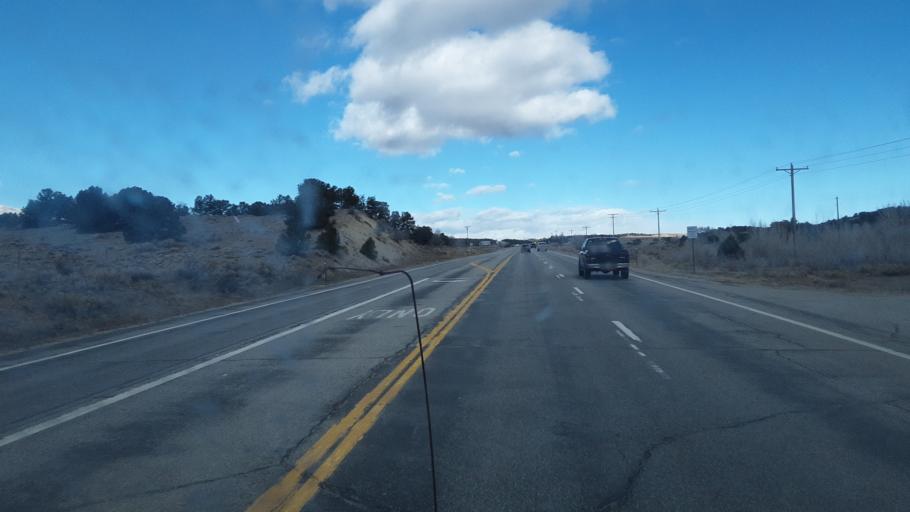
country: US
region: Colorado
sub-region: Chaffee County
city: Salida
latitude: 38.6410
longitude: -106.0829
